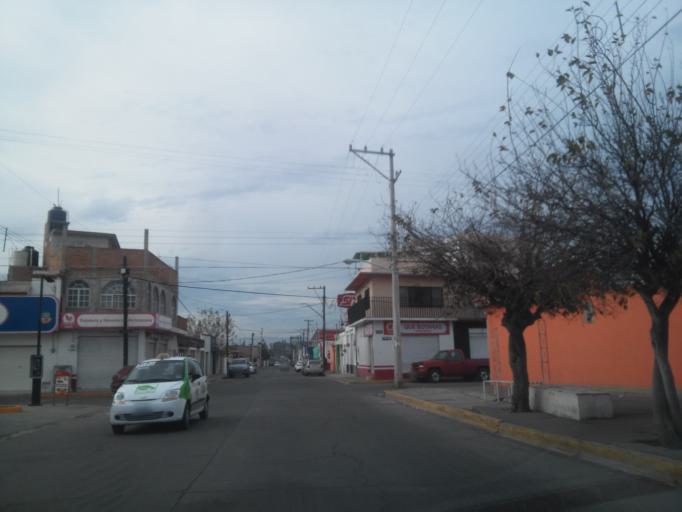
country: MX
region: Durango
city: Victoria de Durango
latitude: 24.0107
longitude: -104.6753
